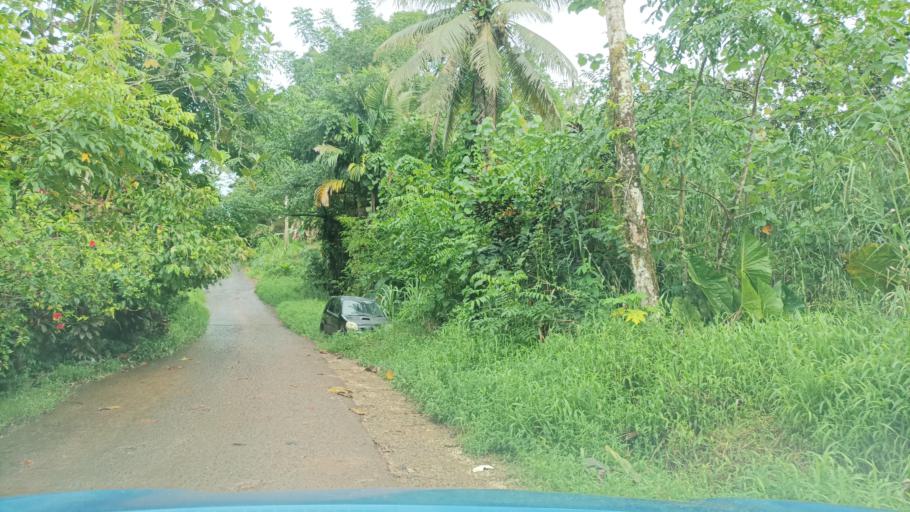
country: FM
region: Pohnpei
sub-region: Sokehs Municipality
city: Palikir - National Government Center
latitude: 6.8770
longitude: 158.1608
